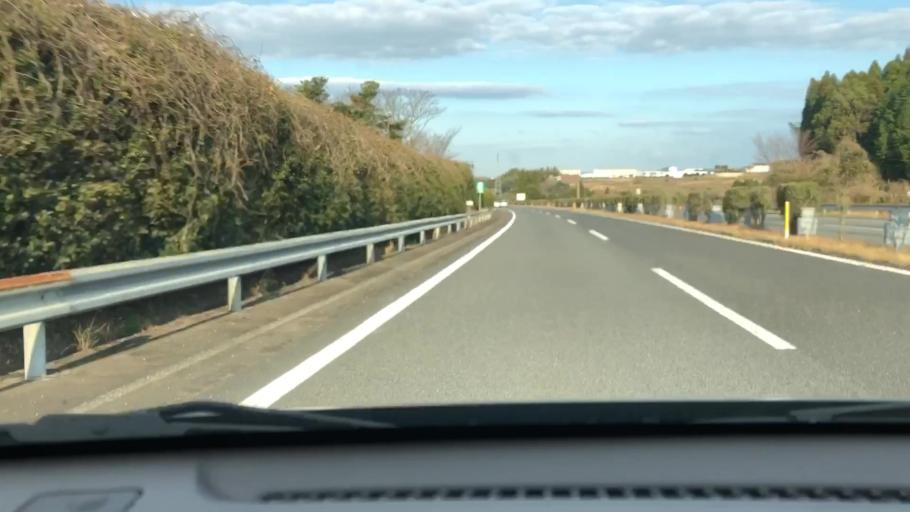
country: JP
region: Miyazaki
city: Miyazaki-shi
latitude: 31.8233
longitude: 131.3060
